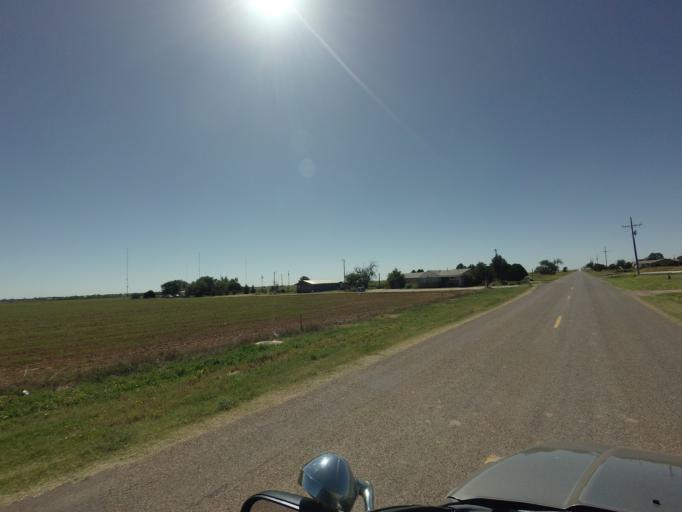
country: US
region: New Mexico
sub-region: Curry County
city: Clovis
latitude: 34.4484
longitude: -103.2066
